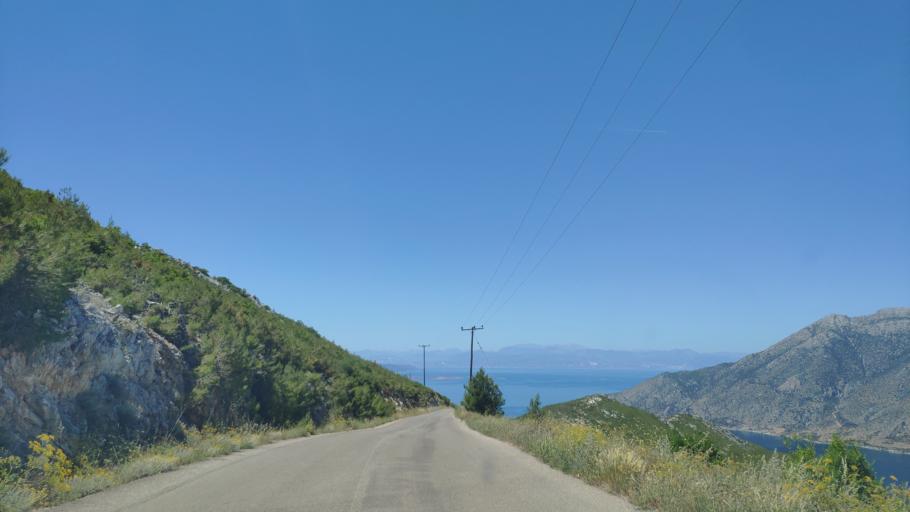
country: GR
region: Central Greece
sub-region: Nomos Voiotias
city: Kaparellion
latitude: 38.1979
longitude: 23.1485
